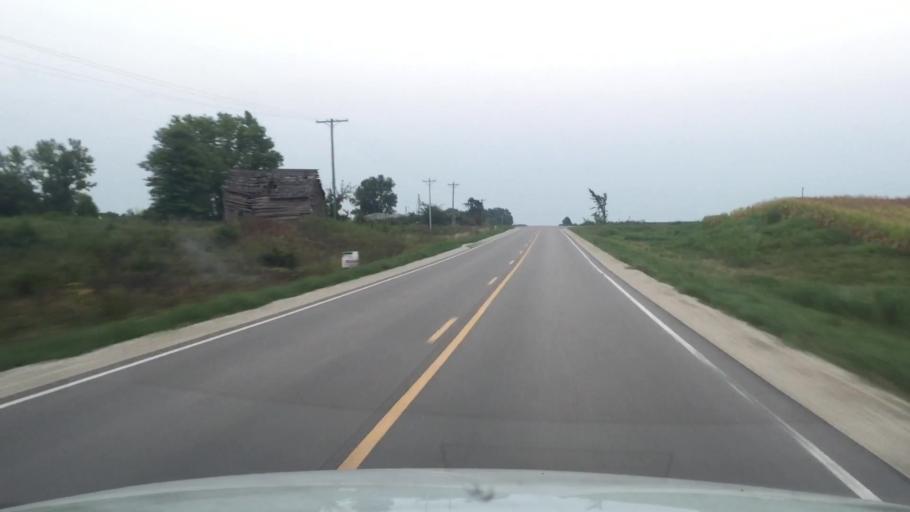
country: US
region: Iowa
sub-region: Warren County
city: Indianola
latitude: 41.1826
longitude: -93.4827
